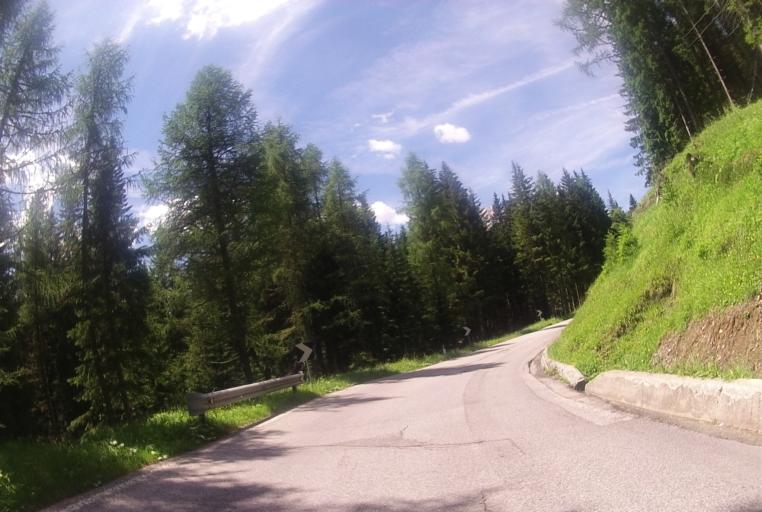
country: IT
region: Veneto
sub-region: Provincia di Belluno
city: Cortina d'Ampezzo
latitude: 46.5641
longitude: 12.2416
